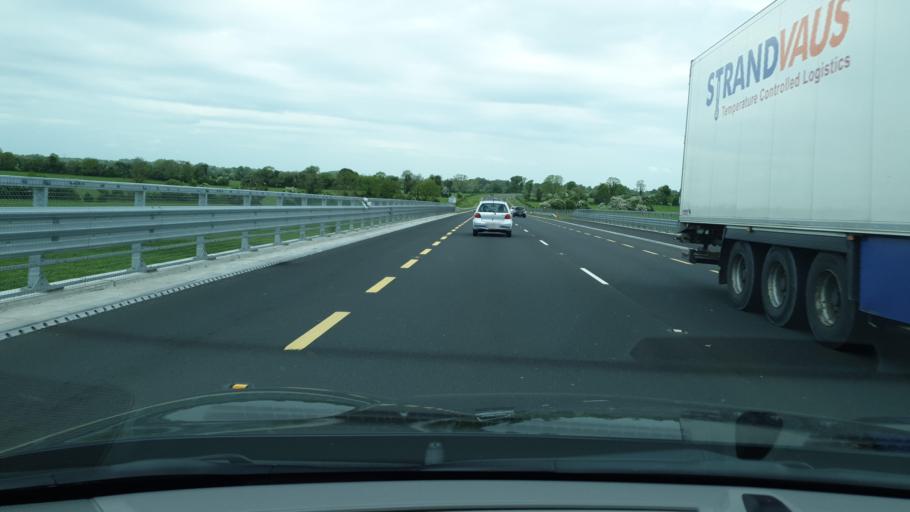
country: IE
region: Leinster
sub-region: Kildare
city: Sallins
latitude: 53.2501
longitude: -6.6806
